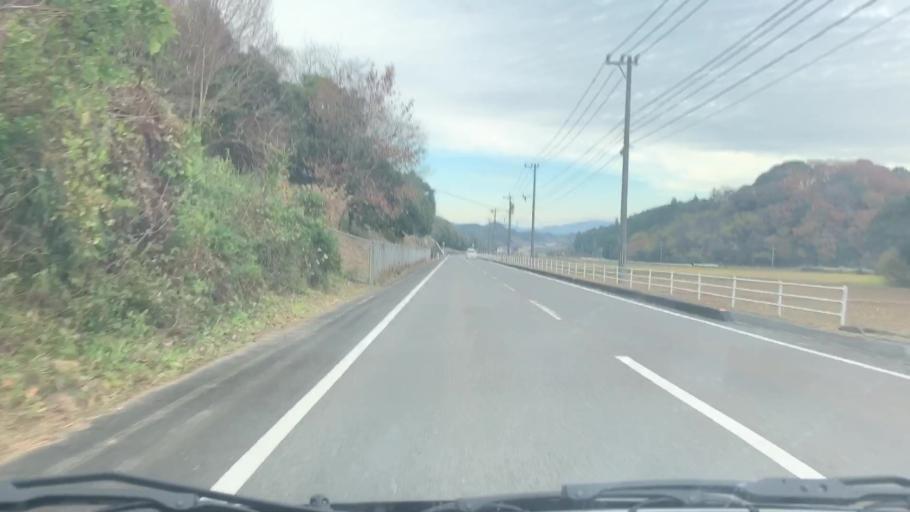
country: JP
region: Saga Prefecture
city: Ureshinomachi-shimojuku
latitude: 33.1186
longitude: 129.9778
